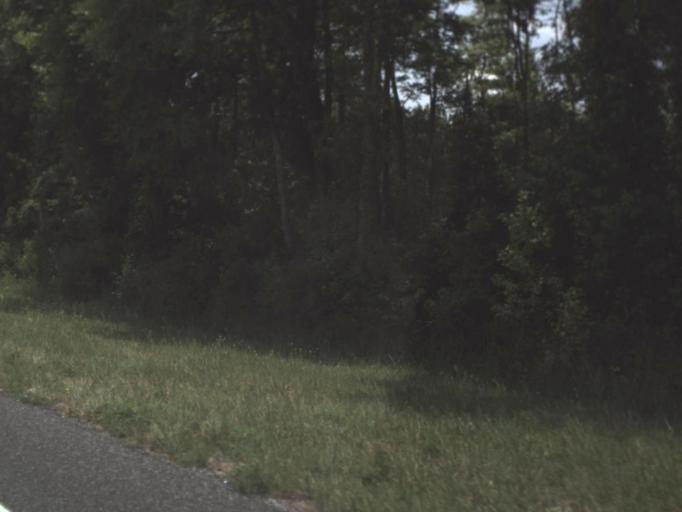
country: US
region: Florida
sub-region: Taylor County
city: Perry
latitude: 29.9266
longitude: -83.4413
